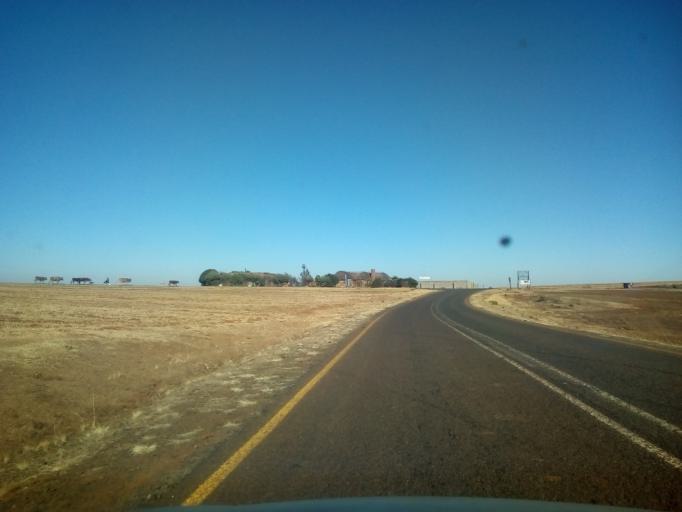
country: LS
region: Berea
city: Teyateyaneng
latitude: -29.2820
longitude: 27.6616
